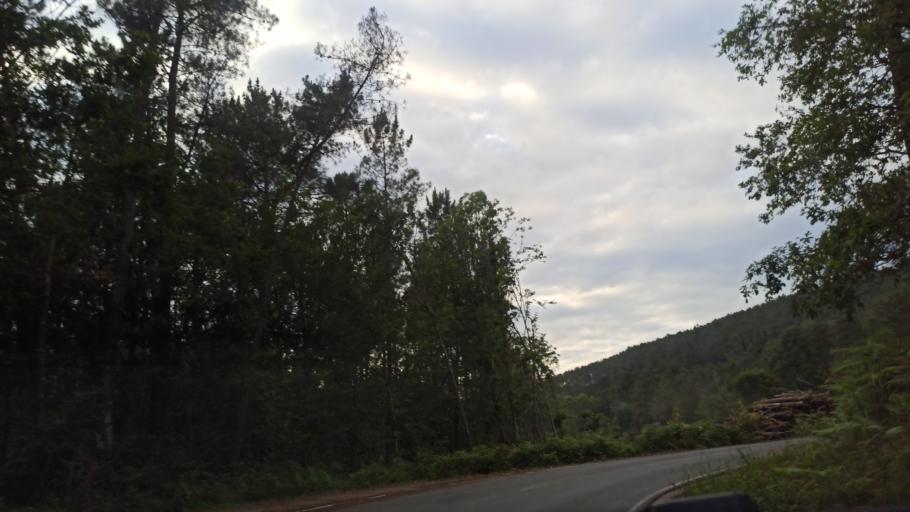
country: ES
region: Galicia
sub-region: Provincia da Coruna
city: Santiso
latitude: 42.8209
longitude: -8.1267
